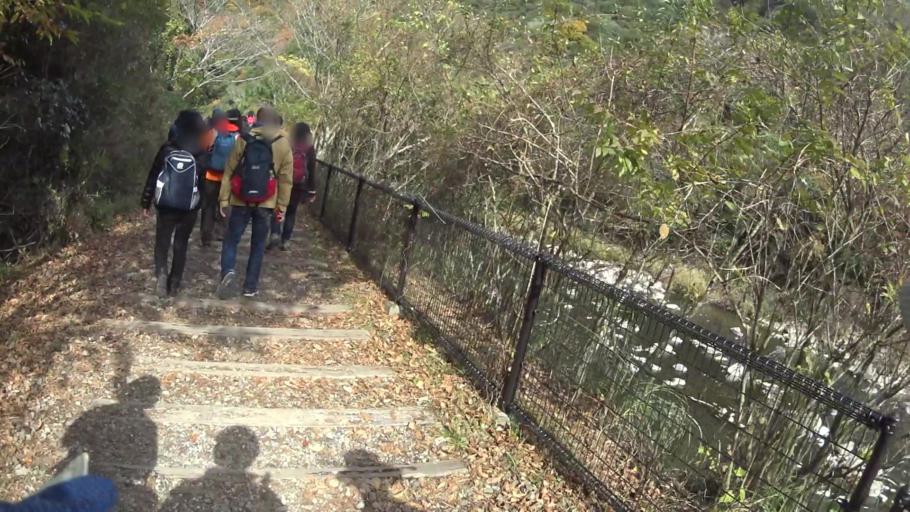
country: JP
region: Hyogo
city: Takarazuka
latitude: 34.8331
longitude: 135.3247
